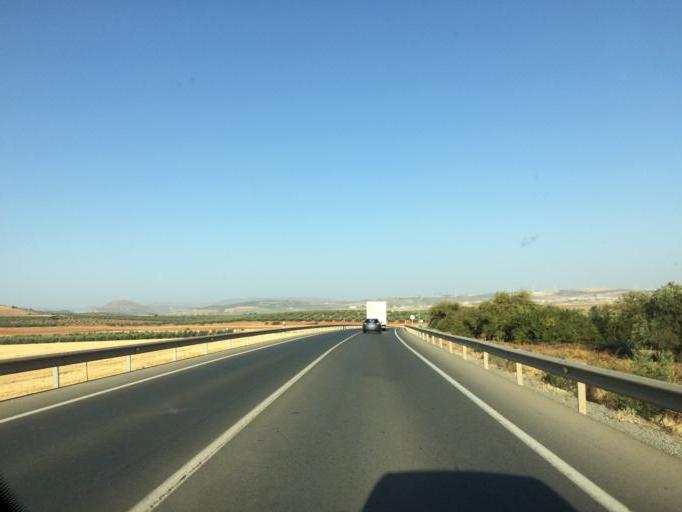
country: ES
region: Andalusia
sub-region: Provincia de Malaga
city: Campillos
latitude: 37.0502
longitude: -4.8164
